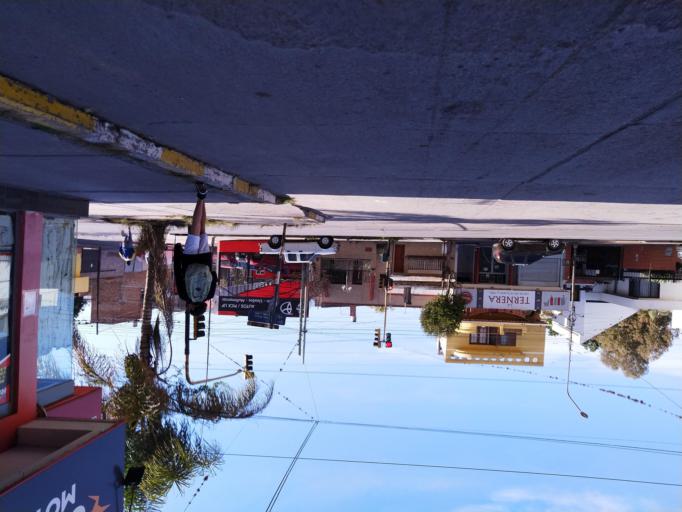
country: AR
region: Jujuy
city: San Salvador de Jujuy
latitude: -24.2015
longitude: -65.2844
